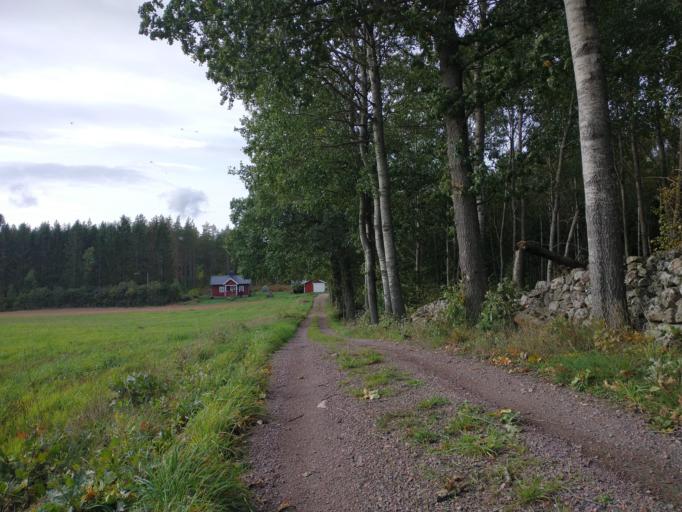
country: SE
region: Kalmar
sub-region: Kalmar Kommun
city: Lindsdal
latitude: 56.7736
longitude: 16.3018
